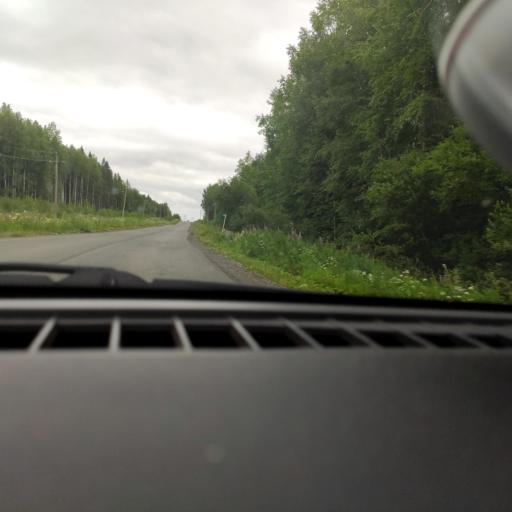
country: RU
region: Perm
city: Polazna
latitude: 58.3319
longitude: 56.1532
